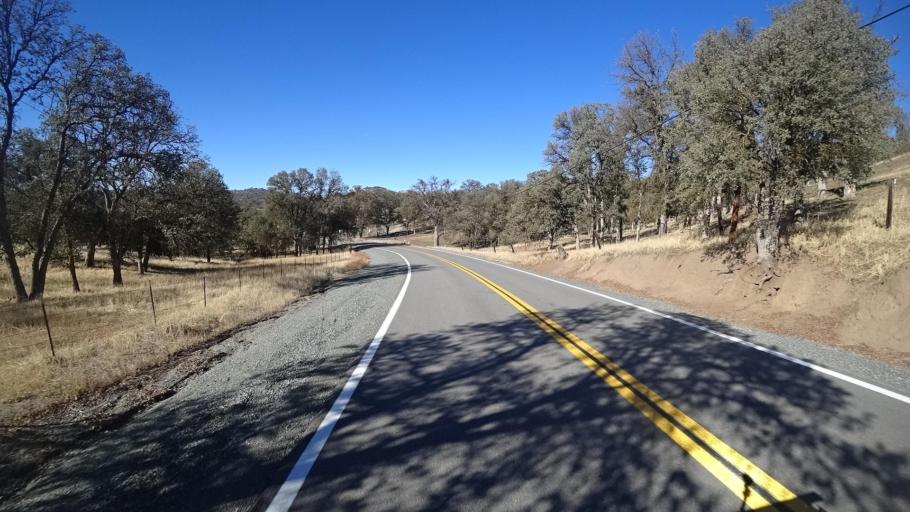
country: US
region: California
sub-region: Kern County
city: Alta Sierra
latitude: 35.7289
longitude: -118.7128
